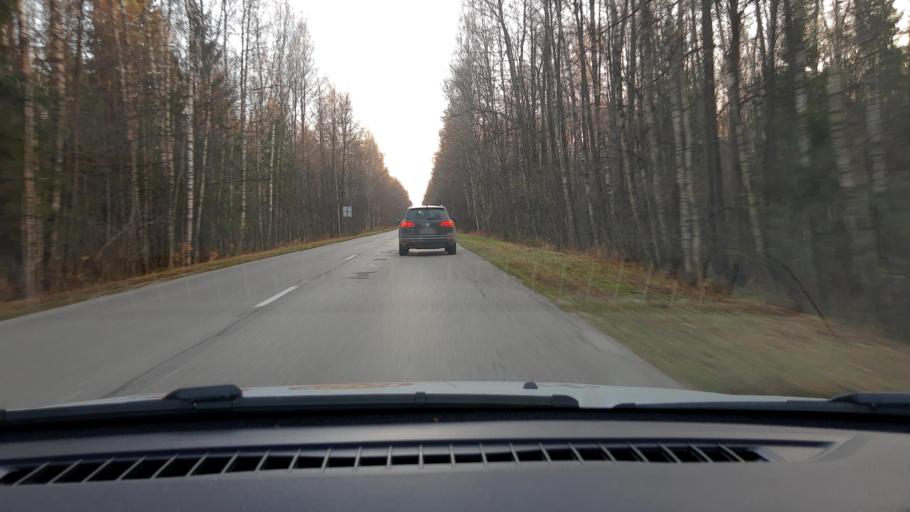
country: RU
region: Nizjnij Novgorod
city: Volodarsk
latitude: 56.2767
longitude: 43.1666
